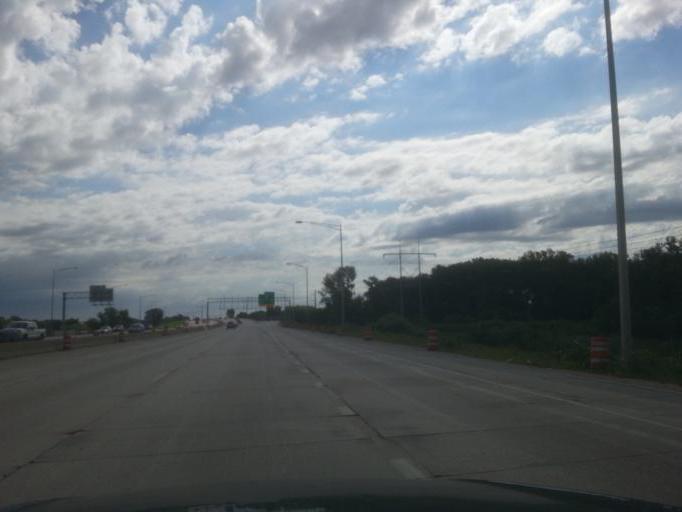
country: US
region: Wisconsin
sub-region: Dane County
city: Monona
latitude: 43.0451
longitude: -89.3144
